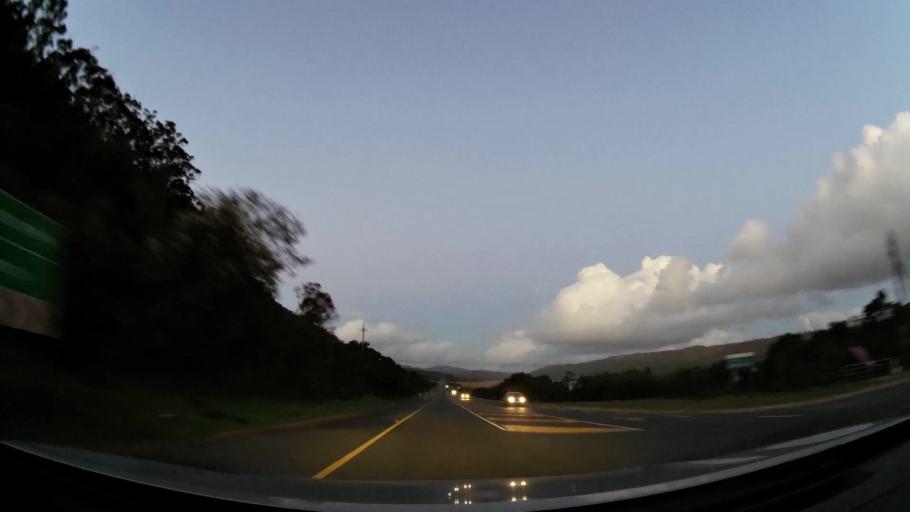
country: ZA
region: Western Cape
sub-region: Eden District Municipality
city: Knysna
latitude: -34.0221
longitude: 22.8337
